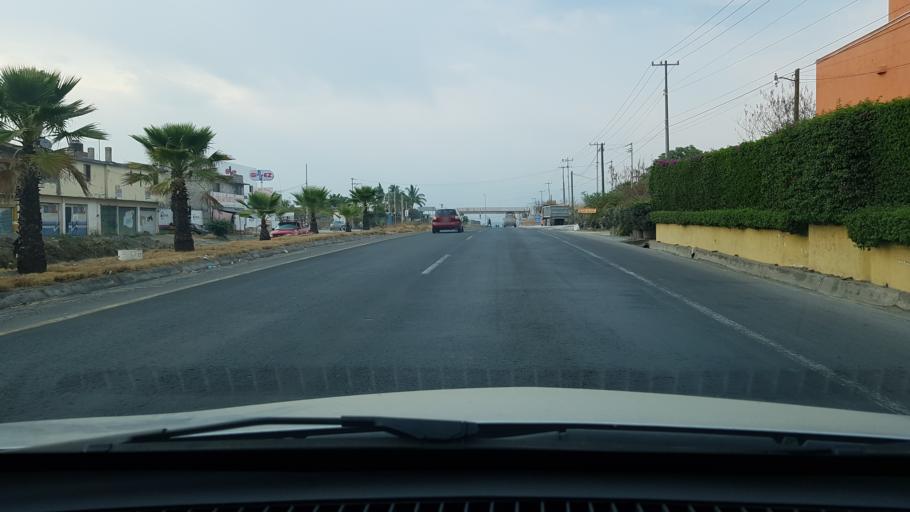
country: MX
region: Morelos
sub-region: Yecapixtla
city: Juan Morales
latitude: 18.8112
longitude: -98.9161
